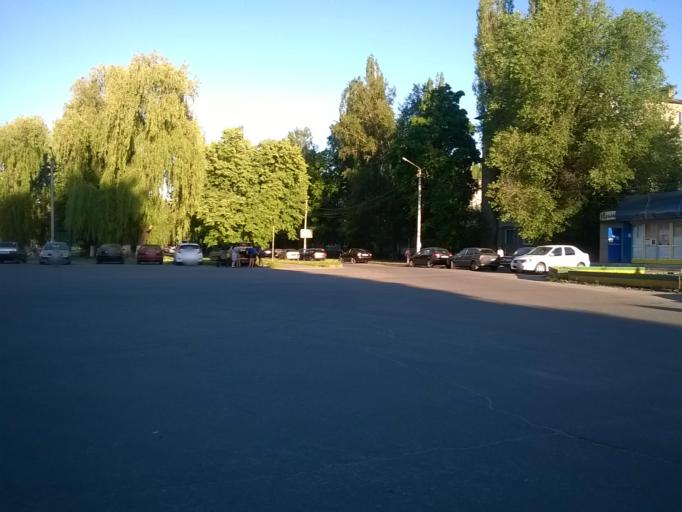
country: RU
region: Kursk
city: Kursk
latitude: 51.6702
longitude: 36.1468
